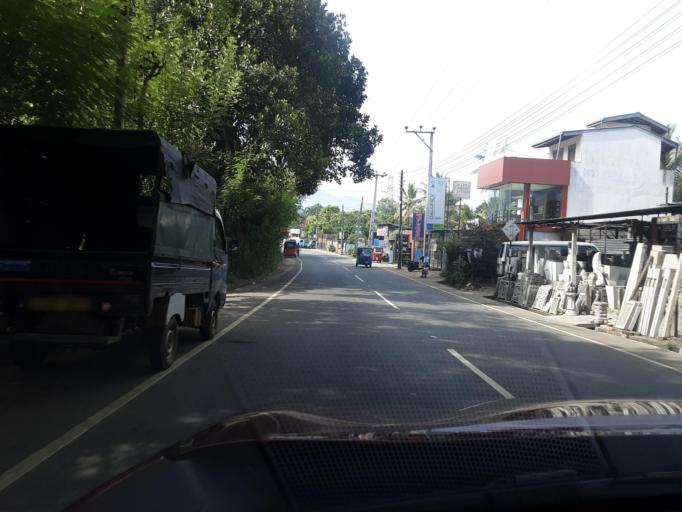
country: LK
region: Uva
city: Badulla
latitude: 6.9841
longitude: 81.0644
